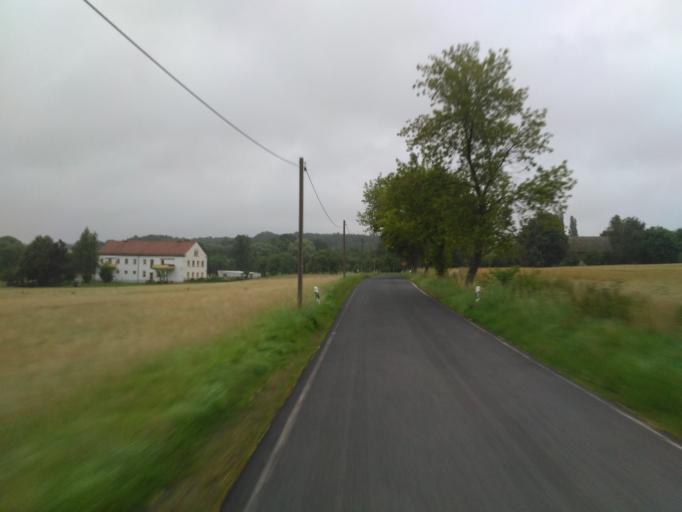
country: DE
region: Saxony
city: Nossen
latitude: 51.0897
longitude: 13.3381
